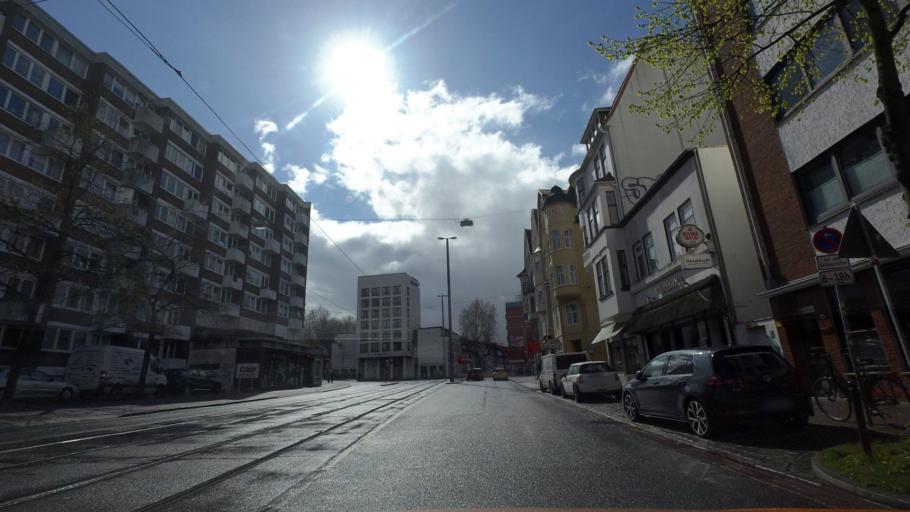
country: DE
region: Bremen
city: Bremen
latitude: 53.0721
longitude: 8.8006
